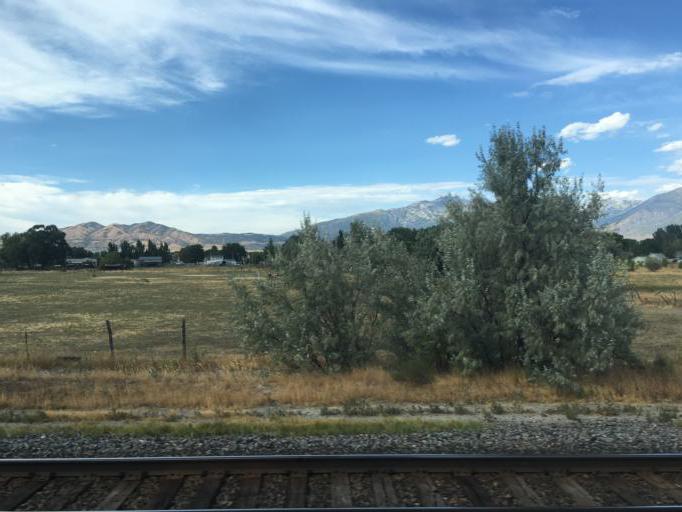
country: US
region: Utah
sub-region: Utah County
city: Lehi
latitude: 40.3804
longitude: -111.8474
